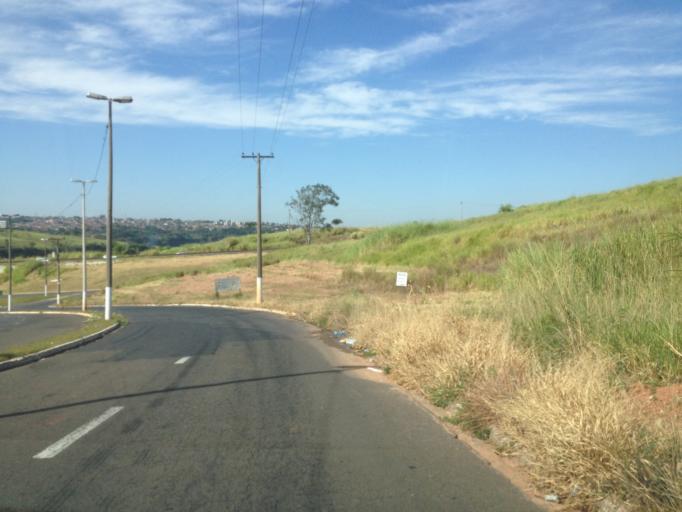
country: BR
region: Sao Paulo
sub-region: Marilia
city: Marilia
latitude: -22.2283
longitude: -49.9505
